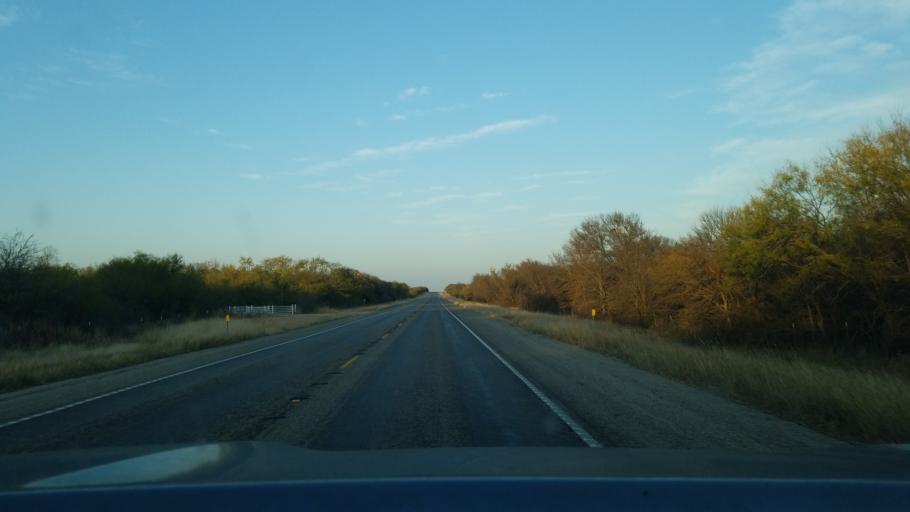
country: US
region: Texas
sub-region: Eastland County
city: Cisco
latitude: 32.4224
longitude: -98.9352
